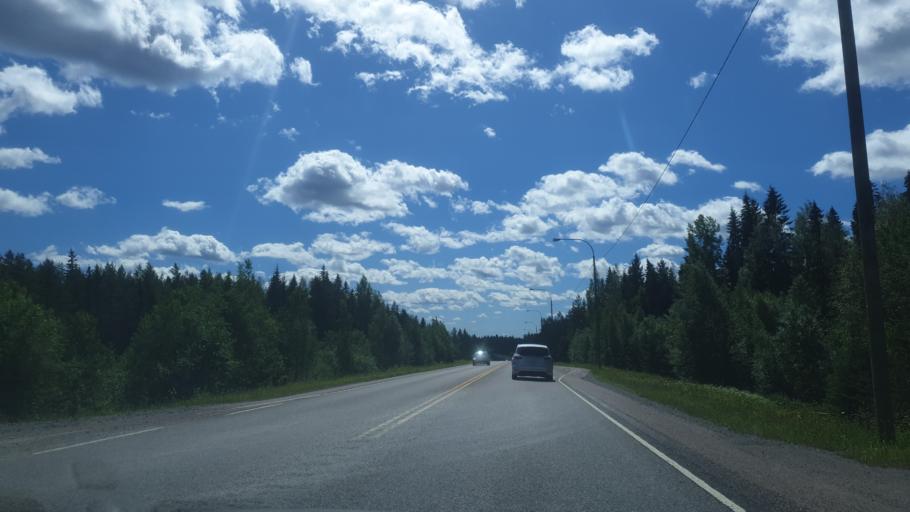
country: FI
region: Northern Savo
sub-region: Varkaus
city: Varkaus
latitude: 62.3682
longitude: 27.8098
